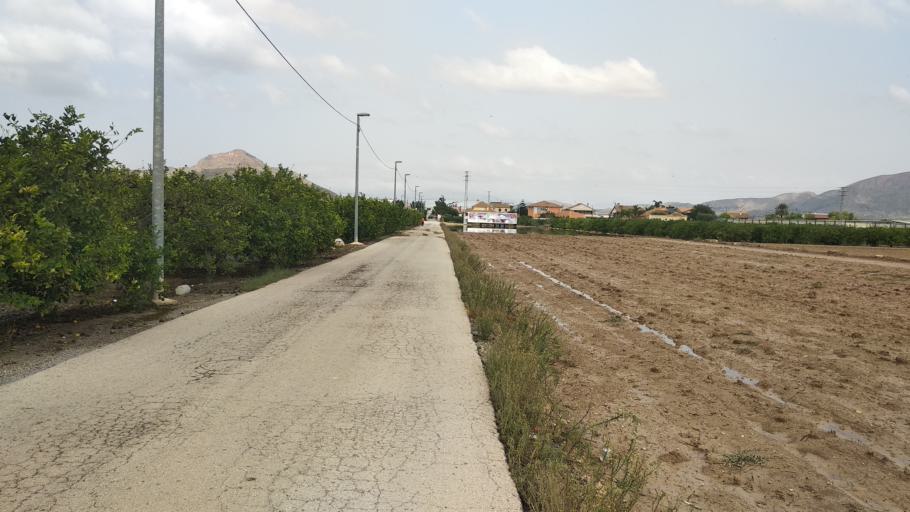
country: ES
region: Murcia
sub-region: Murcia
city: Santomera
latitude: 38.0404
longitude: -1.0403
